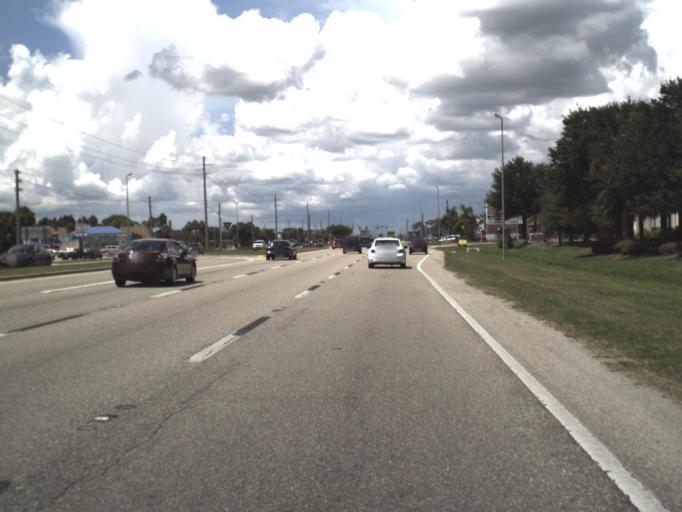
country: US
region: Florida
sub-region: Charlotte County
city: Port Charlotte
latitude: 26.9821
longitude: -82.0987
